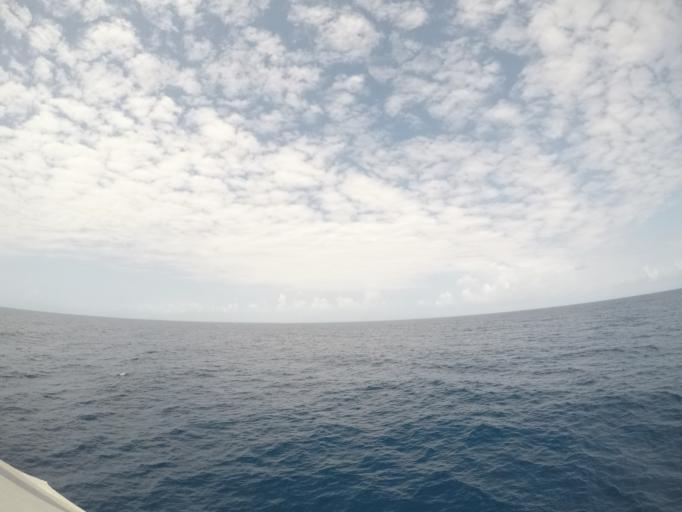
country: TZ
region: Zanzibar North
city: Nungwi
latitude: -5.5844
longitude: 39.3556
